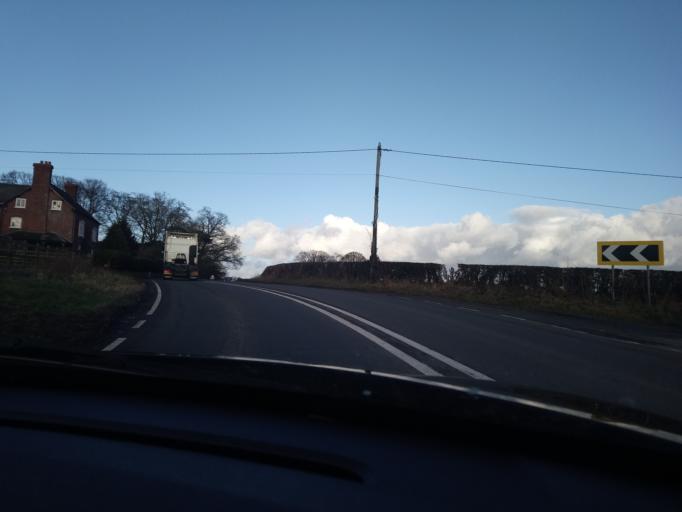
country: GB
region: England
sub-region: Shropshire
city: Ellesmere
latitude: 52.9026
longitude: -2.8640
